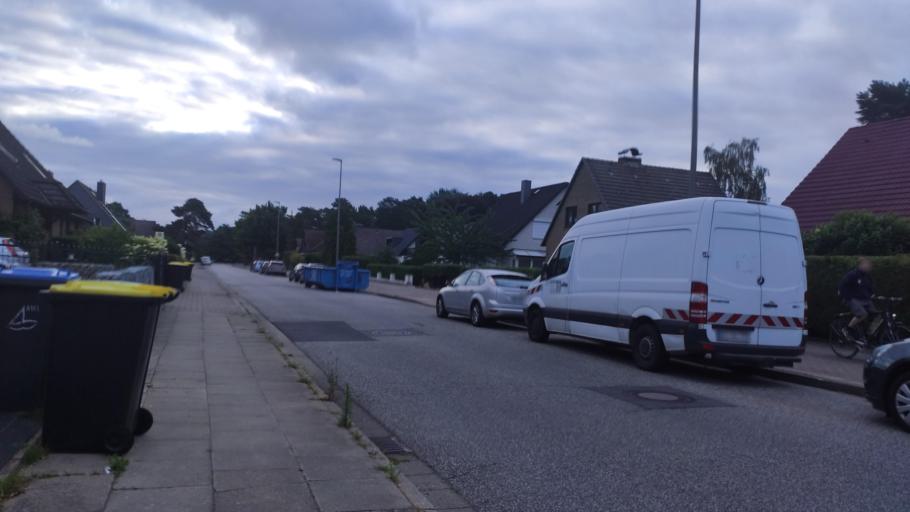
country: DE
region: Schleswig-Holstein
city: Geesthacht
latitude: 53.4401
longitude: 10.3429
